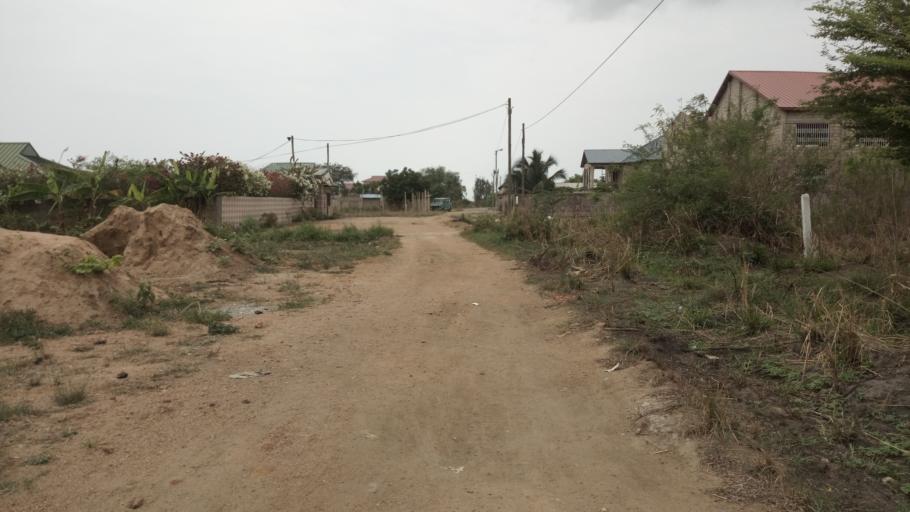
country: GH
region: Central
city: Winneba
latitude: 5.3815
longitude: -0.6392
